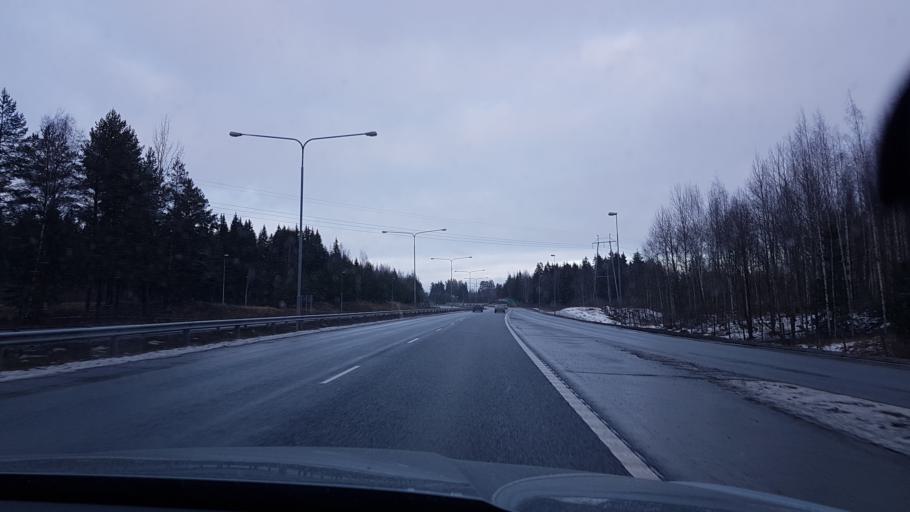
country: FI
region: Pirkanmaa
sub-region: Tampere
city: Tampere
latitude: 61.4988
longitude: 23.8857
